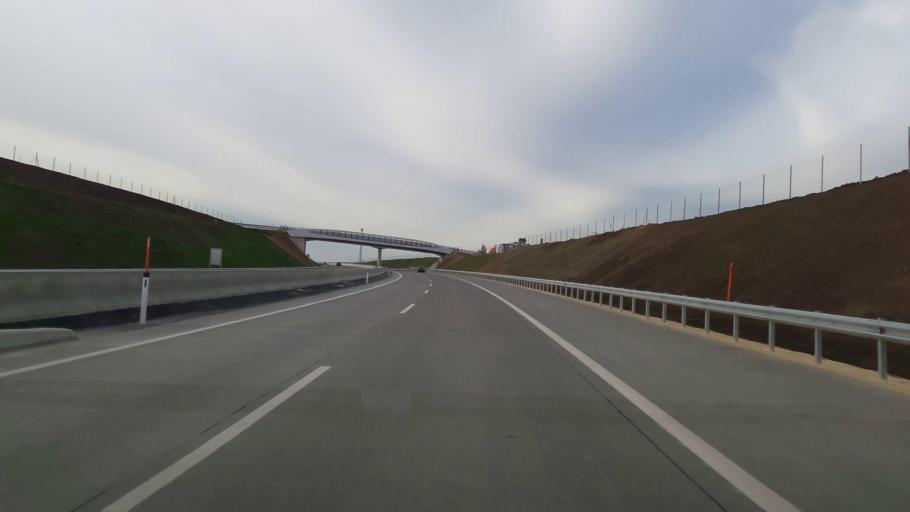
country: AT
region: Lower Austria
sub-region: Politischer Bezirk Mistelbach
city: Herrnbaumgarten
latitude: 48.6725
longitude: 16.6747
